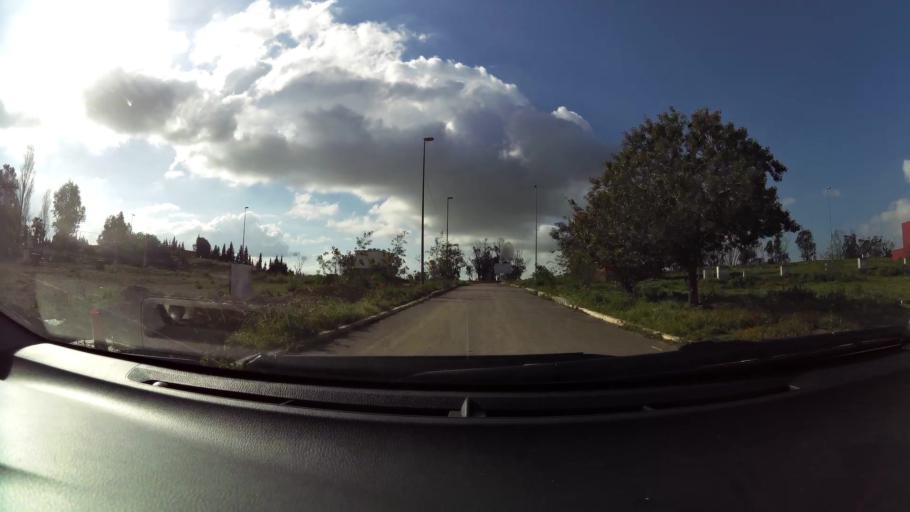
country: MA
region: Chaouia-Ouardigha
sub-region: Settat Province
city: Settat
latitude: 33.0119
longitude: -7.6360
